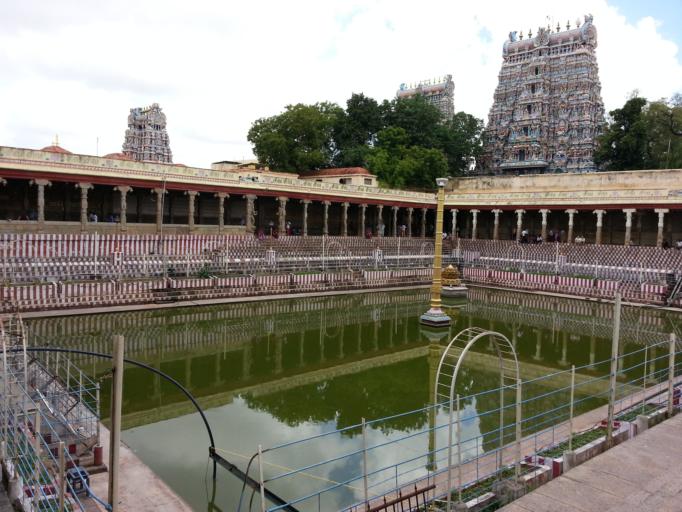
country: IN
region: Tamil Nadu
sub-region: Madurai
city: Madurai
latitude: 9.9208
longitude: 78.1184
